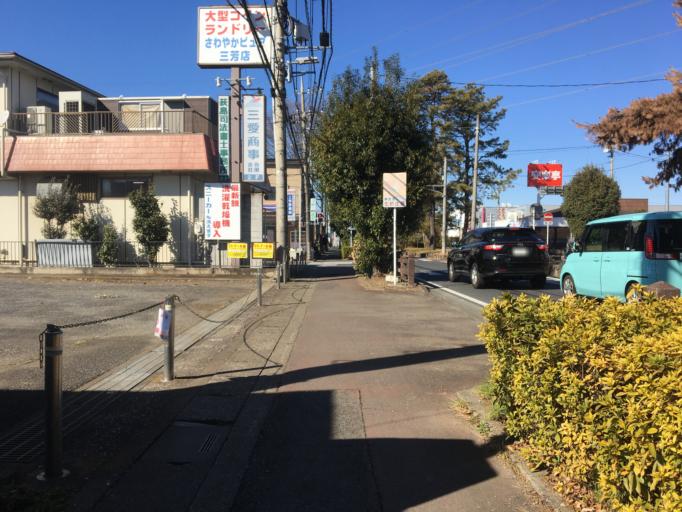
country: JP
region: Saitama
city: Oi
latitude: 35.8429
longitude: 139.5224
